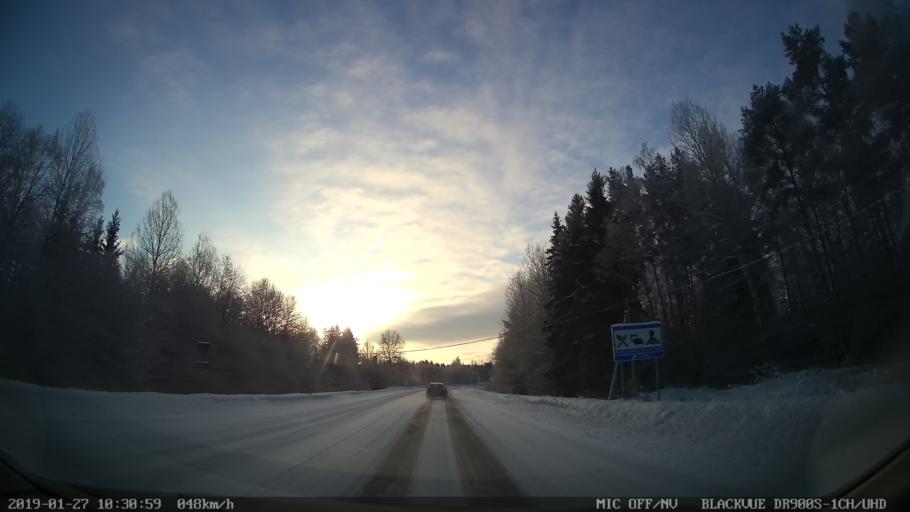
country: EE
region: Harju
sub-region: Raasiku vald
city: Raasiku
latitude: 59.4335
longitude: 25.1932
